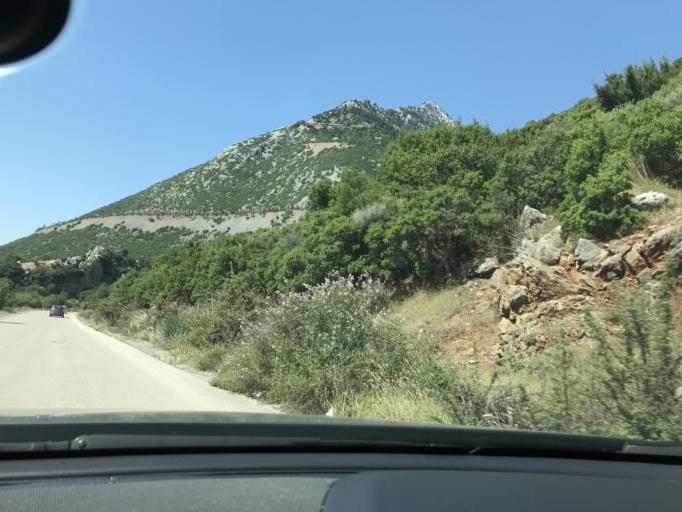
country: GR
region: Central Greece
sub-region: Nomos Voiotias
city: Distomo
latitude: 38.4773
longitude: 22.6847
